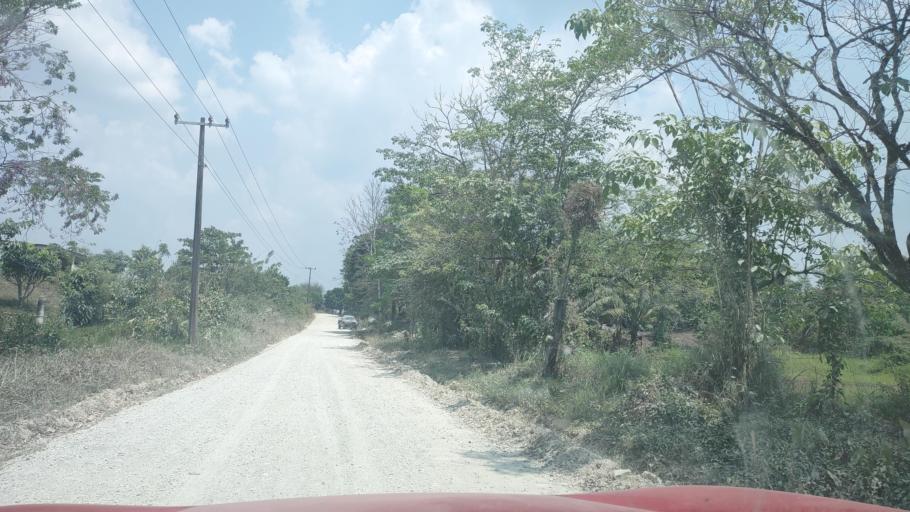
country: MX
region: Tabasco
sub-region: Huimanguillo
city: Francisco Rueda
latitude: 17.6129
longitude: -93.9153
